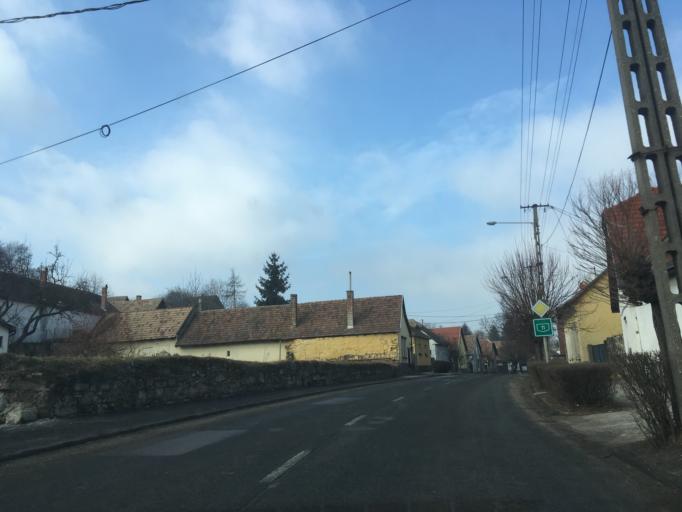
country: HU
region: Komarom-Esztergom
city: Pilismarot
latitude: 47.7649
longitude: 18.9075
